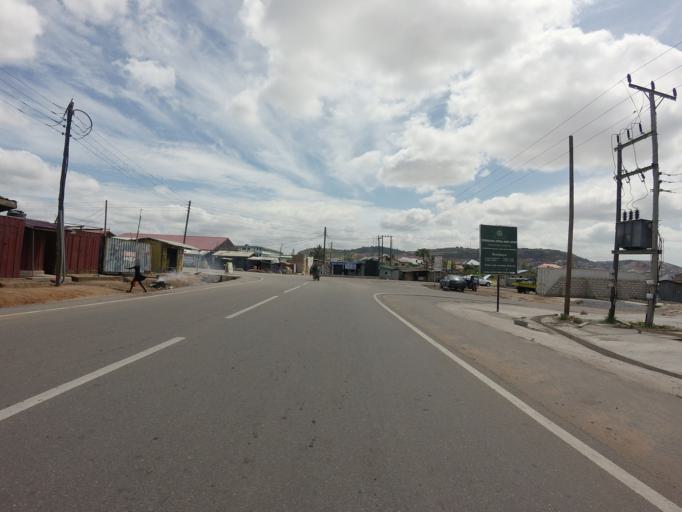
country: GH
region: Central
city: Kasoa
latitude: 5.5357
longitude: -0.3996
